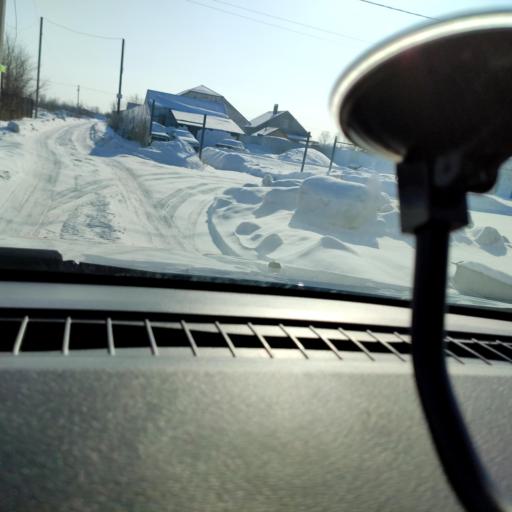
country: RU
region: Samara
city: Samara
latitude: 53.1361
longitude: 50.2524
